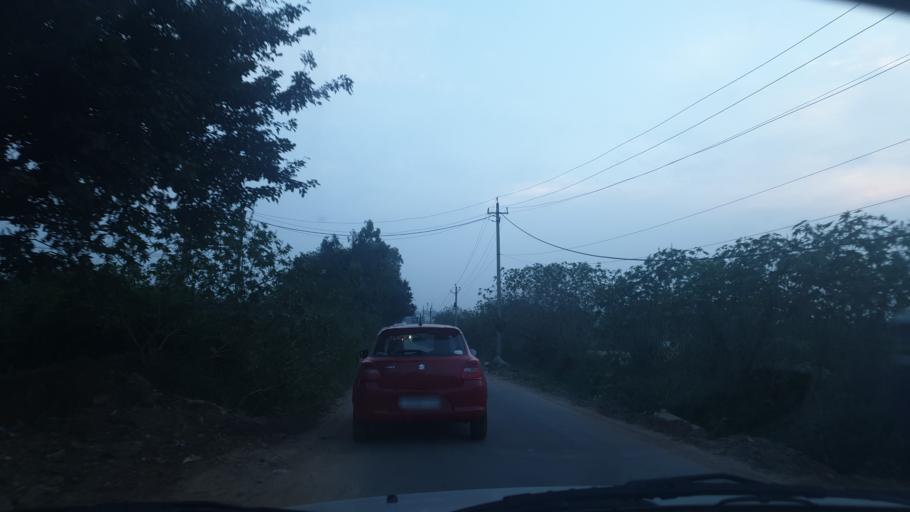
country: IN
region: Karnataka
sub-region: Bangalore Urban
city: Yelahanka
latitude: 13.0547
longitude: 77.6825
